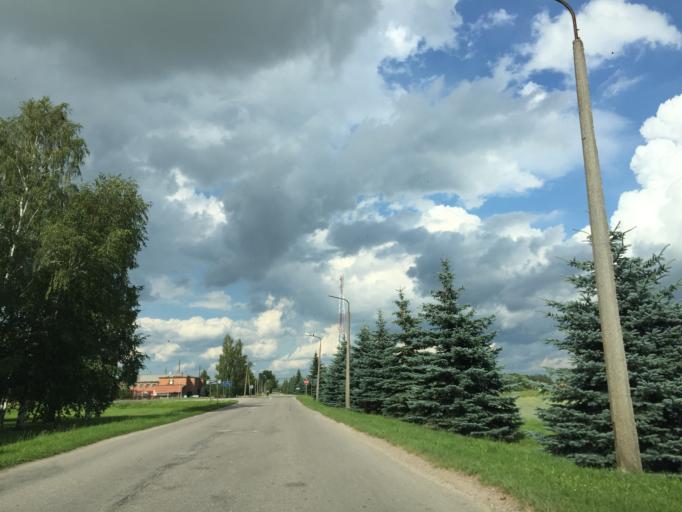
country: LV
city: Tervete
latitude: 56.6213
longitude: 23.4443
